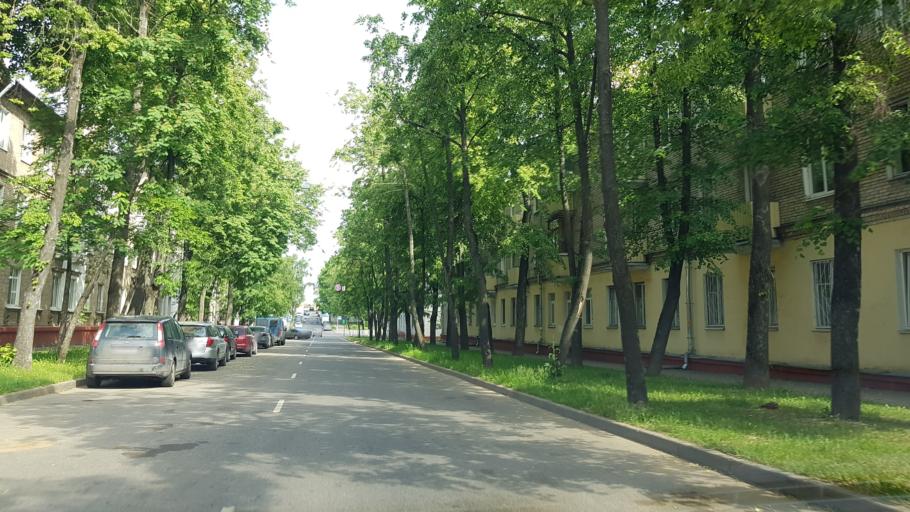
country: BY
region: Minsk
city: Minsk
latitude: 53.8929
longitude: 27.5227
